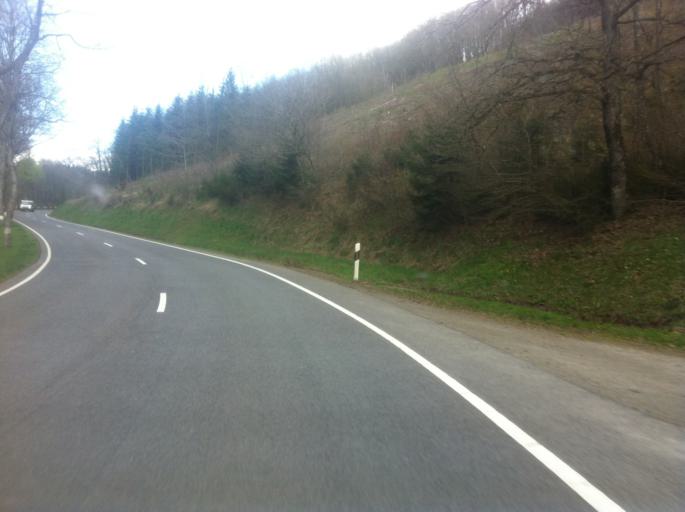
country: LU
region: Diekirch
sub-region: Canton de Wiltz
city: Eschweiler
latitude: 49.9778
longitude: 5.9576
